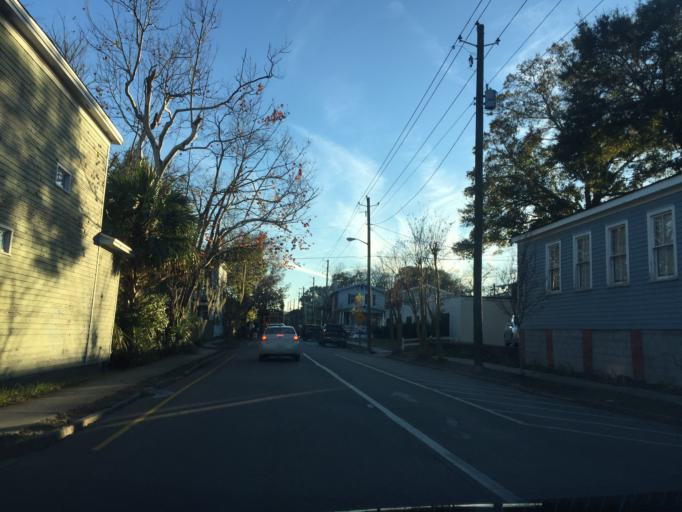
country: US
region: Georgia
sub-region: Chatham County
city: Savannah
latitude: 32.0590
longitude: -81.0936
